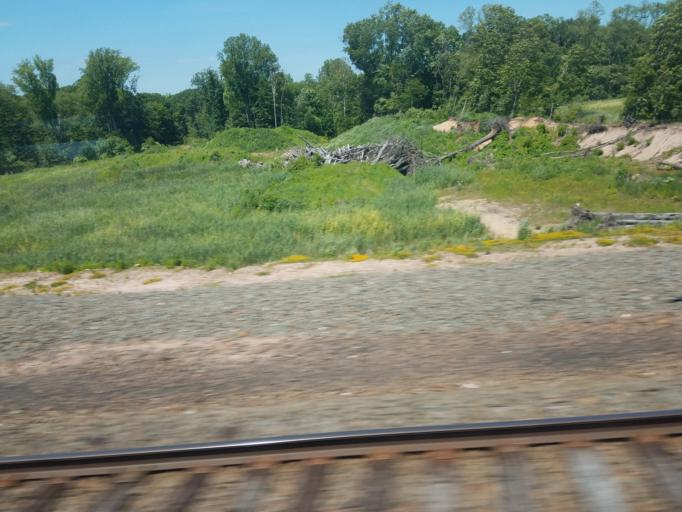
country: US
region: Connecticut
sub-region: New Haven County
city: North Haven
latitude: 41.4086
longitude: -72.8462
